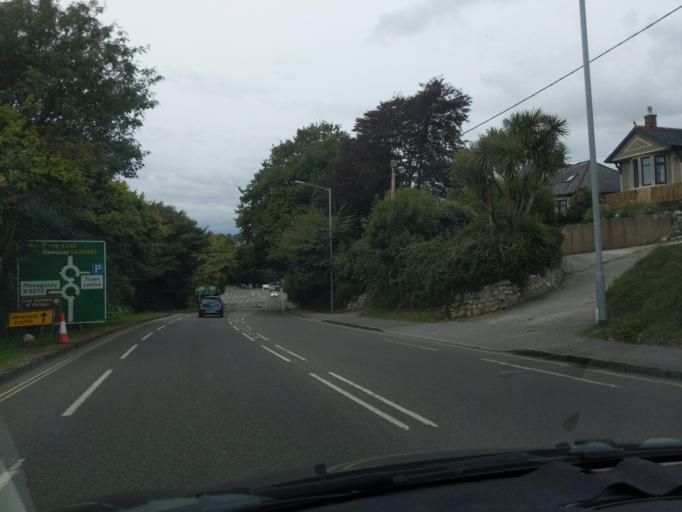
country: GB
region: England
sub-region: Cornwall
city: St Austell
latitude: 50.3338
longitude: -4.7915
